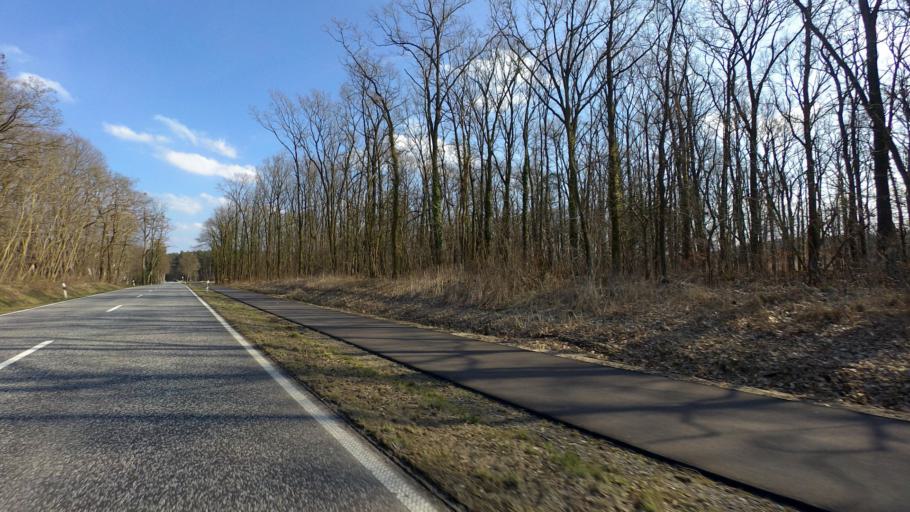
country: DE
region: Brandenburg
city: Trebbin
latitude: 52.2108
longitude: 13.1284
